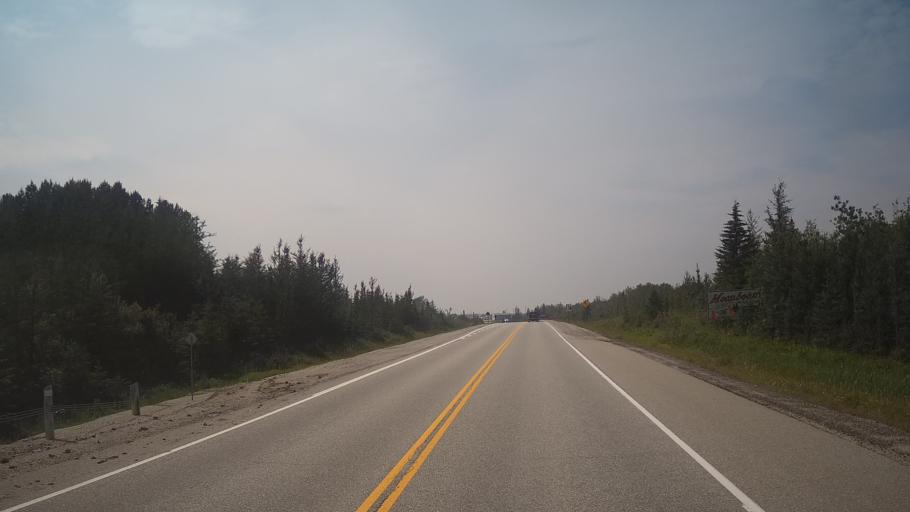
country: CA
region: Ontario
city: Kapuskasing
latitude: 49.3308
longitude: -82.0819
